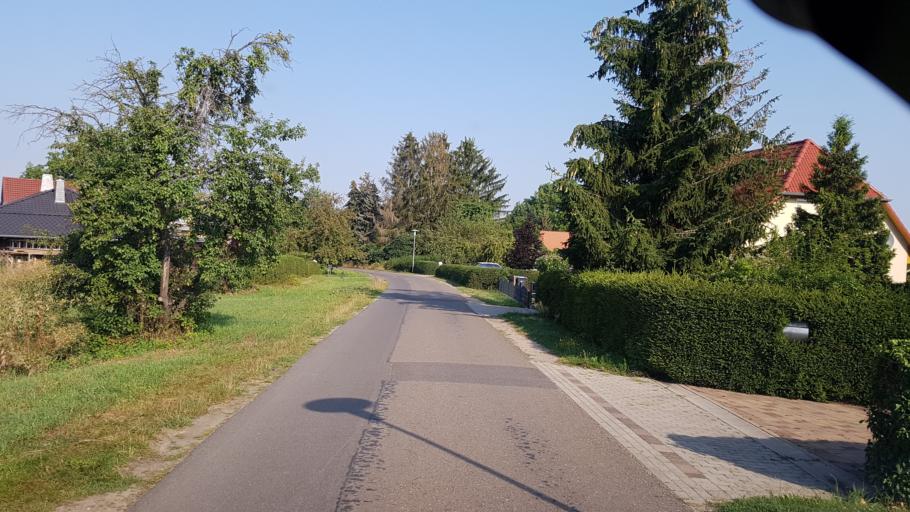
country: DE
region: Brandenburg
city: Drebkau
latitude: 51.6914
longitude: 14.2519
